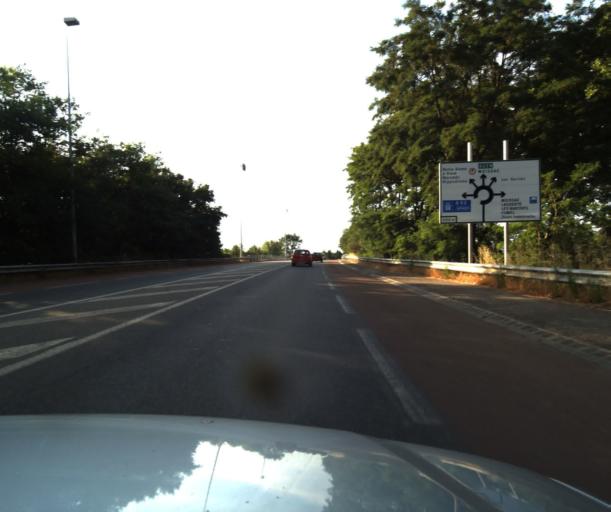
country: FR
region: Midi-Pyrenees
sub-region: Departement du Tarn-et-Garonne
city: Castelsarrasin
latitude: 44.0537
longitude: 1.1005
